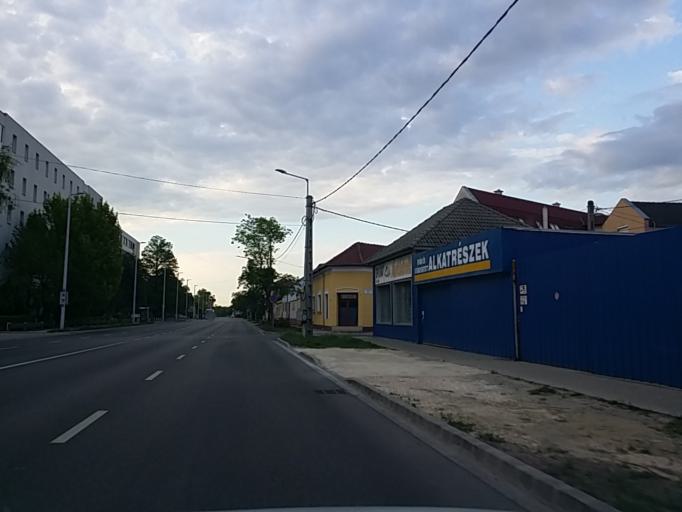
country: HU
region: Bacs-Kiskun
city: Kecskemet
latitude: 46.9078
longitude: 19.7028
